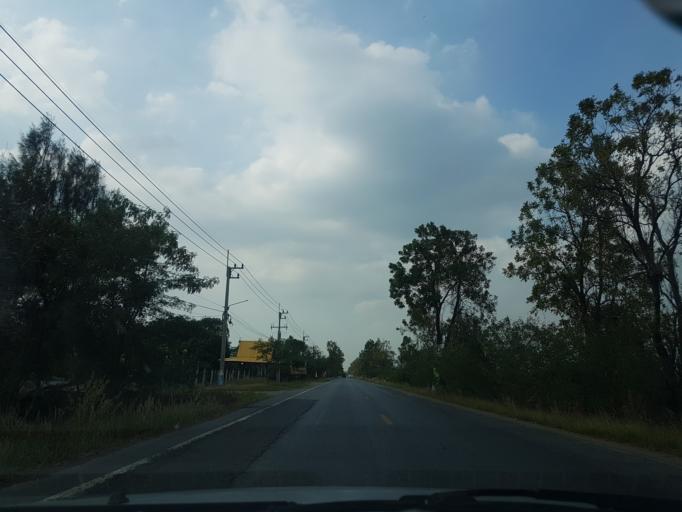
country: TH
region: Phra Nakhon Si Ayutthaya
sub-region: Amphoe Tha Ruea
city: Tha Ruea
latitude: 14.5417
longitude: 100.7379
